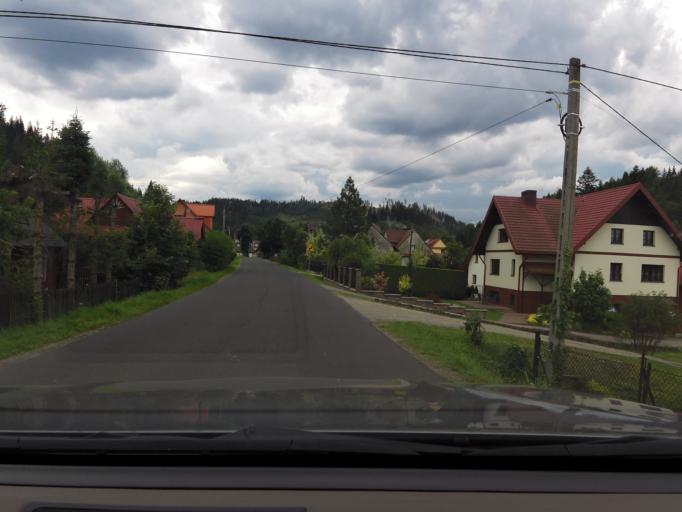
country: PL
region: Silesian Voivodeship
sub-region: Powiat zywiecki
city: Ujsoly
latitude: 49.4718
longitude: 19.1499
